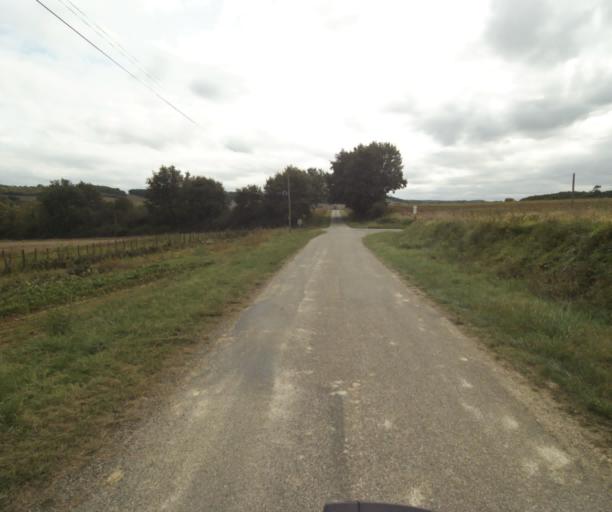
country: FR
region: Midi-Pyrenees
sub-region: Departement du Tarn-et-Garonne
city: Beaumont-de-Lomagne
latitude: 43.8231
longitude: 1.0845
